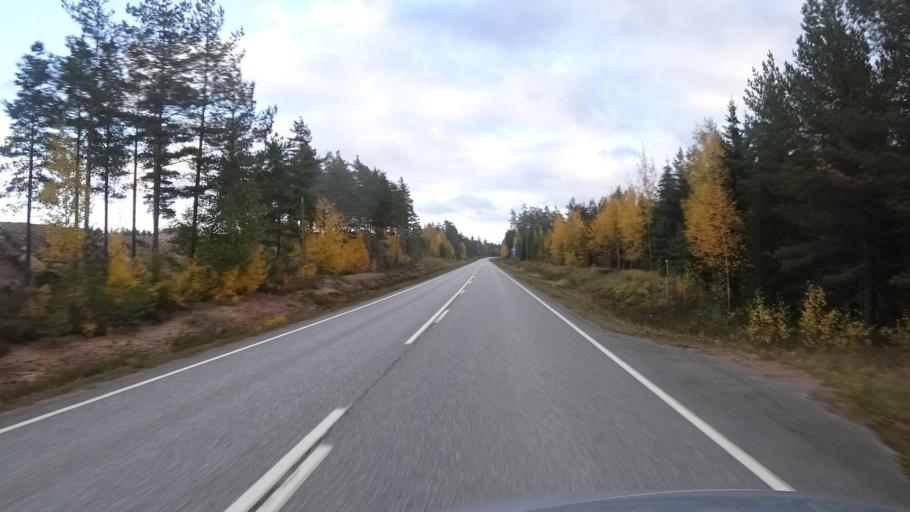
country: FI
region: Satakunta
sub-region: Pori
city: Vampula
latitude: 60.9798
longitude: 22.5642
